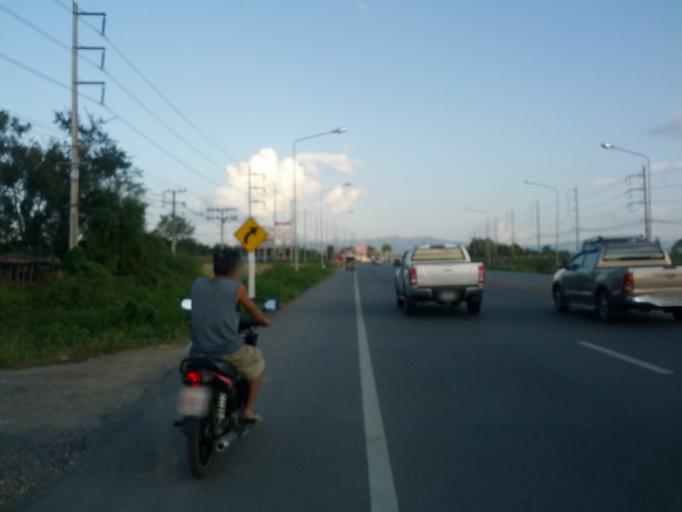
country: TH
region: Chiang Mai
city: San Kamphaeng
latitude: 18.7460
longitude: 99.0722
